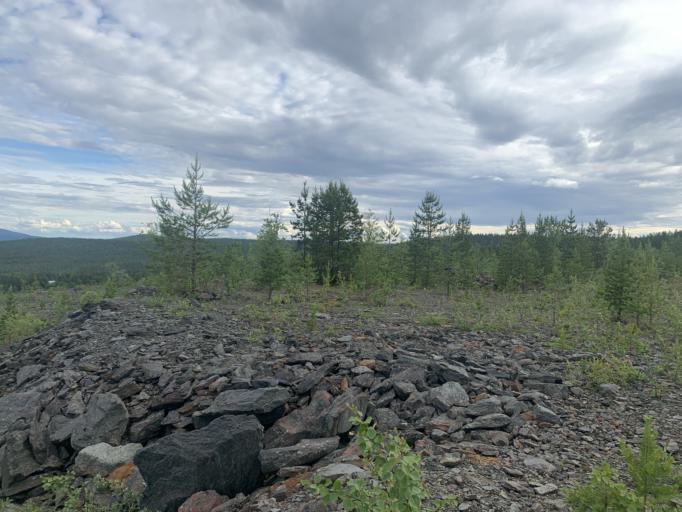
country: RU
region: Murmansk
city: Monchegorsk
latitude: 67.8731
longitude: 33.0868
